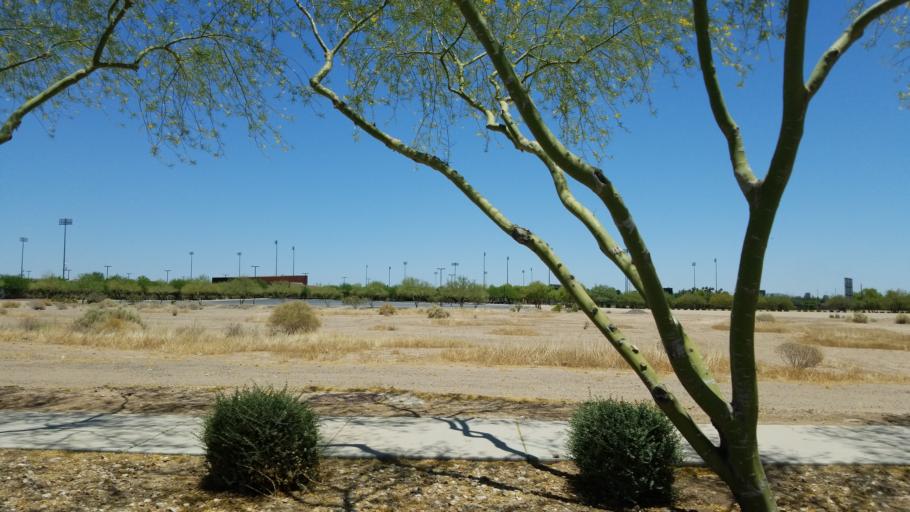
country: US
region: Arizona
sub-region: Maricopa County
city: Litchfield Park
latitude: 33.5111
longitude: -112.2998
